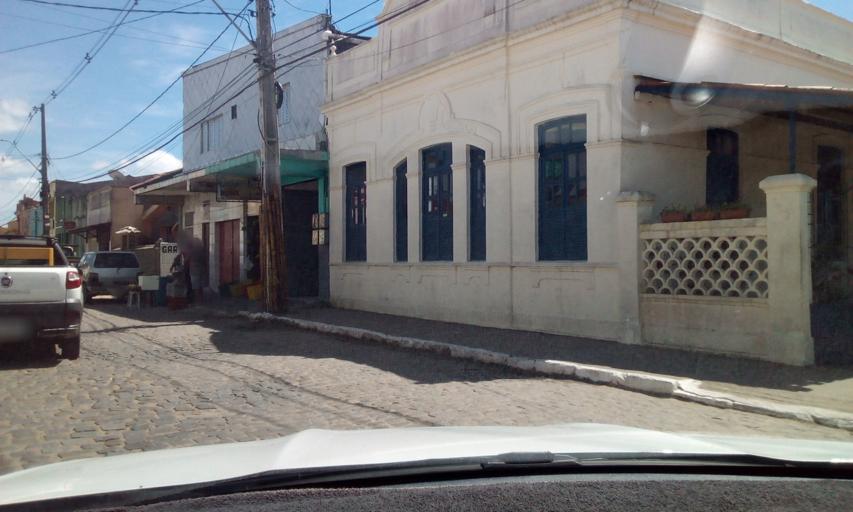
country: BR
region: Paraiba
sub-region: Areia
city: Areia
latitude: -6.9677
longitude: -35.7009
